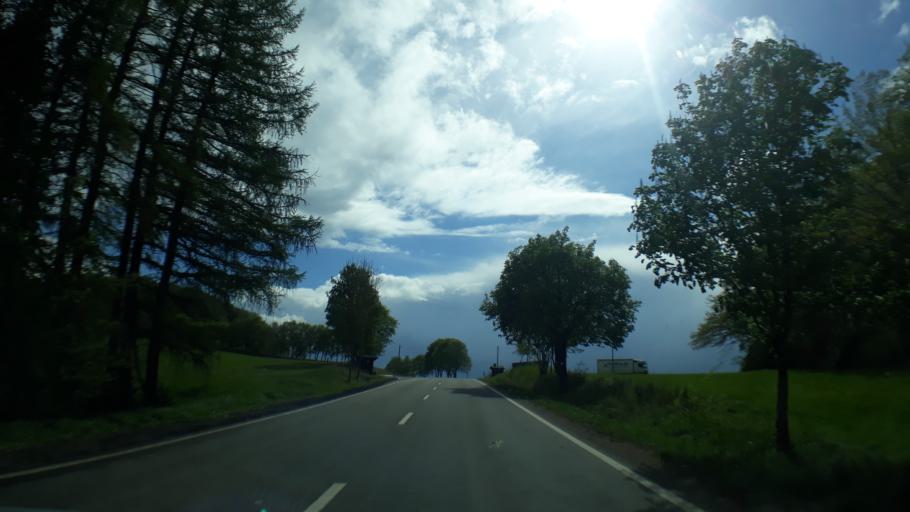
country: DE
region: North Rhine-Westphalia
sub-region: Regierungsbezirk Koln
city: Kall
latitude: 50.5094
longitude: 6.5396
